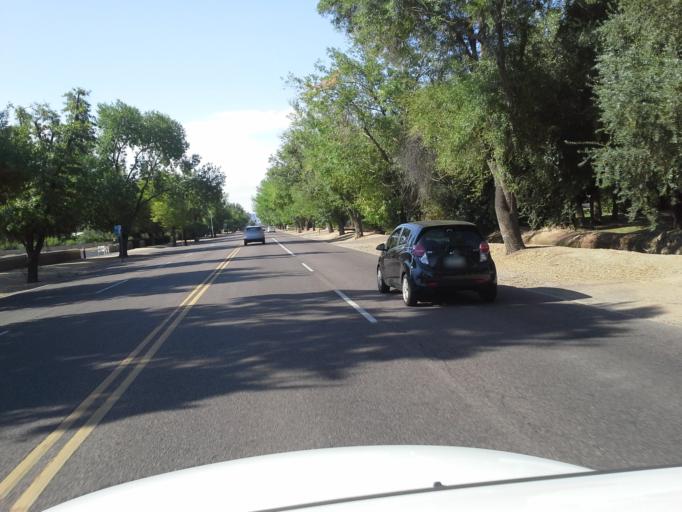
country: US
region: Arizona
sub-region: Maricopa County
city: Phoenix
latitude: 33.5287
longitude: -112.0738
